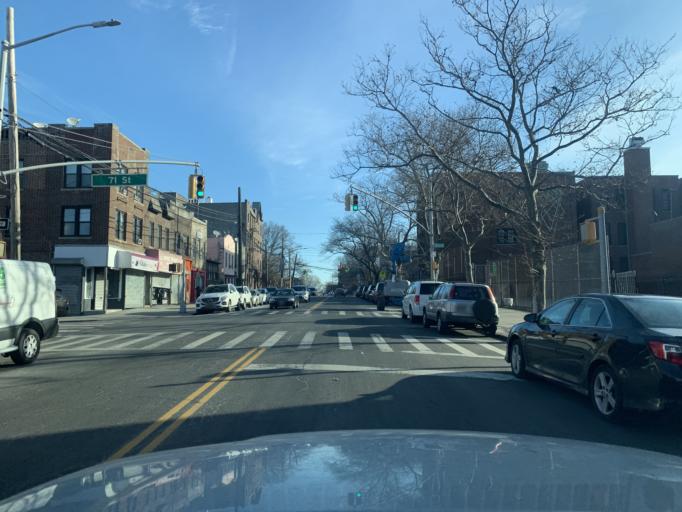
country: US
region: New York
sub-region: Queens County
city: Long Island City
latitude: 40.7425
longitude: -73.8941
